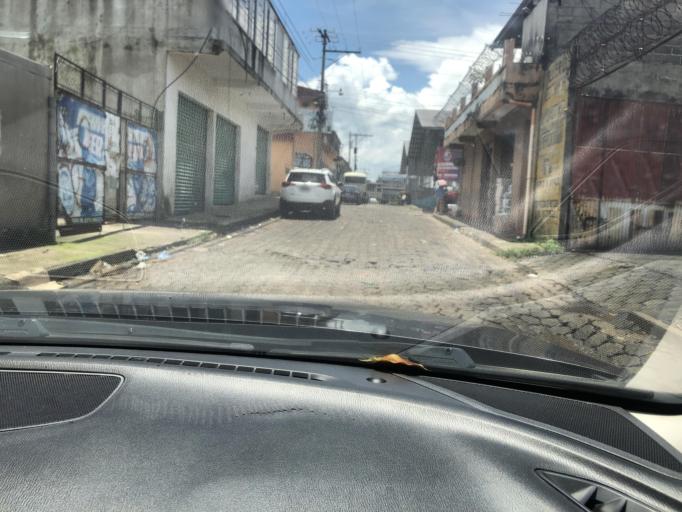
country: GT
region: Quetzaltenango
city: Coatepeque
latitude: 14.7062
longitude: -91.8675
